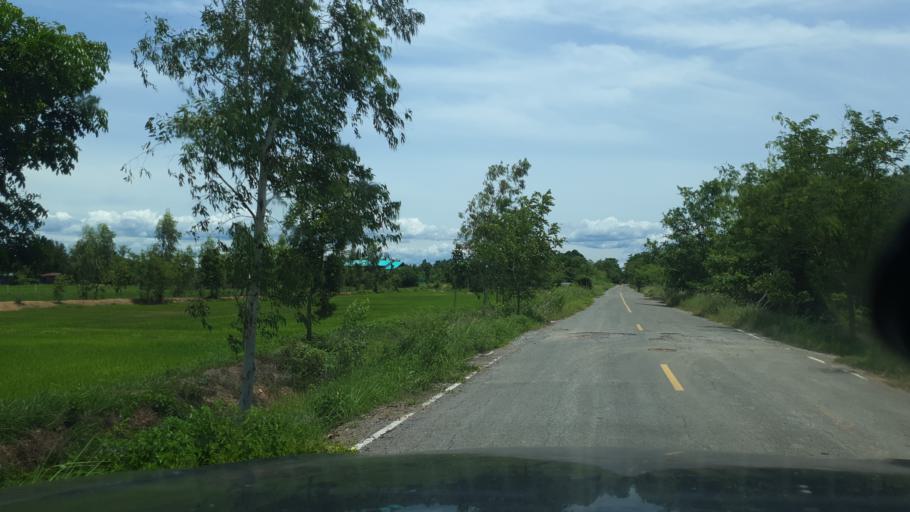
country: TH
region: Sukhothai
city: Ban Na
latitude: 17.1040
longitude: 99.6788
